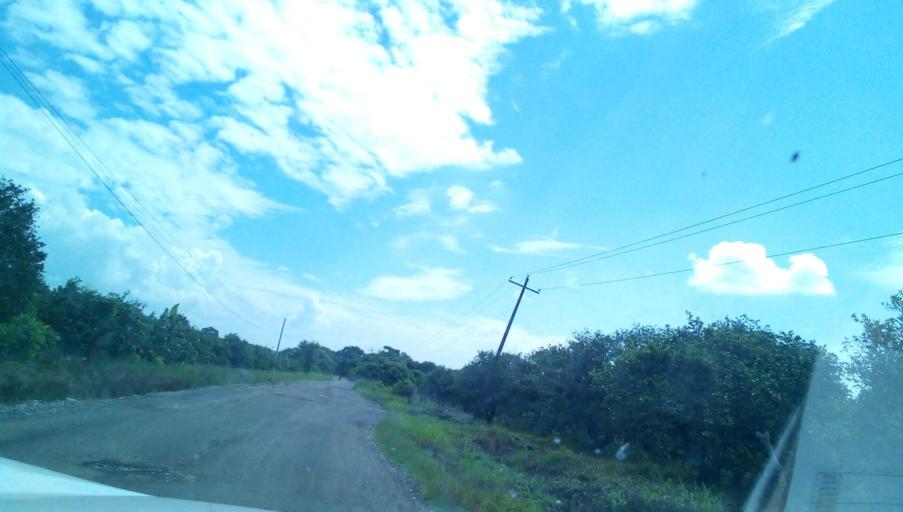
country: MX
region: Veracruz
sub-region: Alamo Temapache
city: Vegas de la Soledad y Soledad Dos
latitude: 20.9046
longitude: -97.9347
